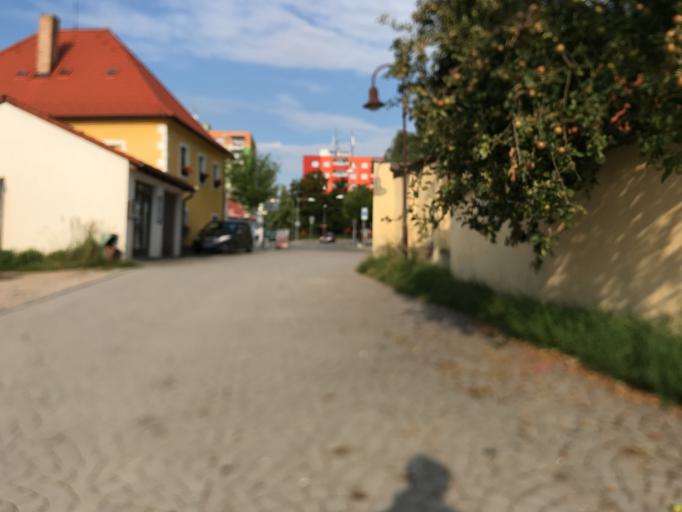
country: CZ
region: Jihocesky
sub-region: Okres Jindrichuv Hradec
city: Trebon
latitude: 49.0035
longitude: 14.7654
